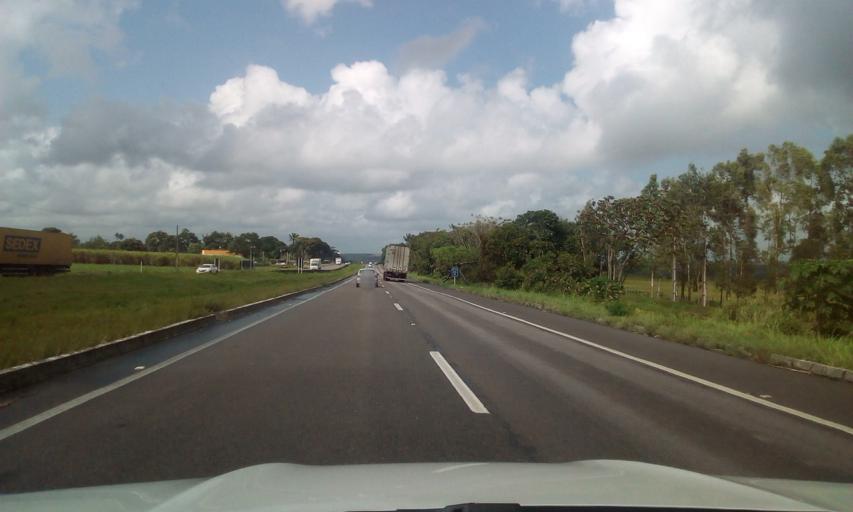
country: BR
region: Paraiba
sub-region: Alhandra
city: Alhandra
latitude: -7.3603
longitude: -34.9516
